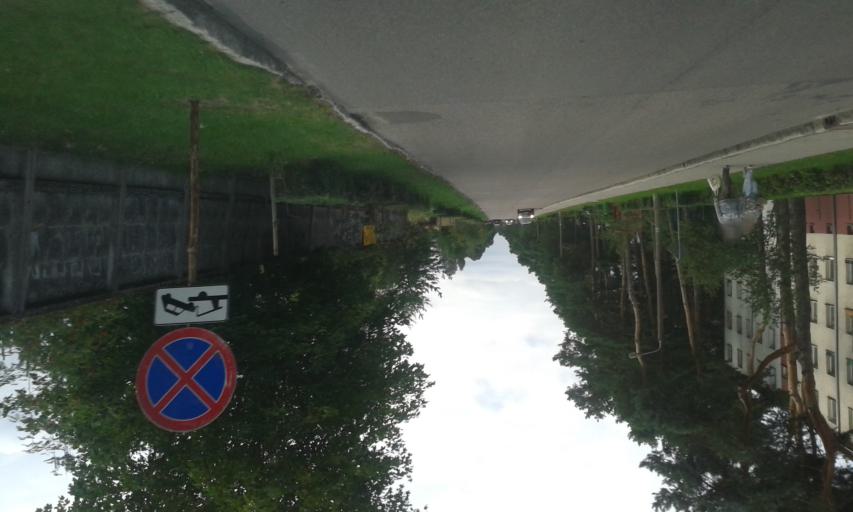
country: PL
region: West Pomeranian Voivodeship
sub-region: Powiat szczecinecki
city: Borne Sulinowo
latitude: 53.5812
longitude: 16.5335
